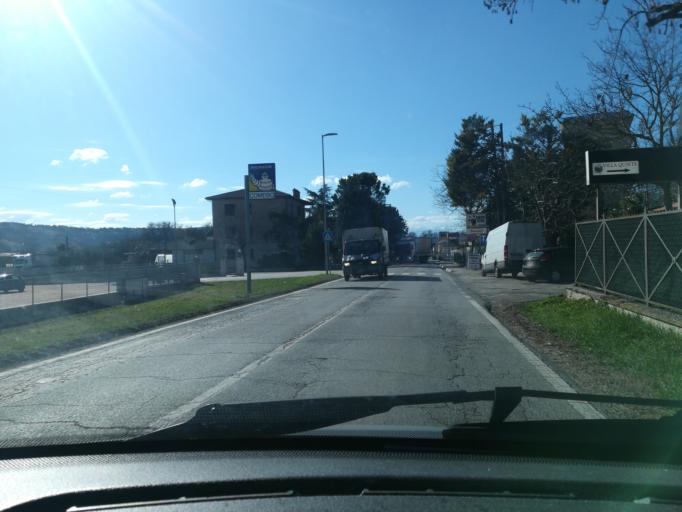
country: IT
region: The Marches
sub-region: Provincia di Macerata
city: Montecassiano
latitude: 43.3481
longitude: 13.4348
